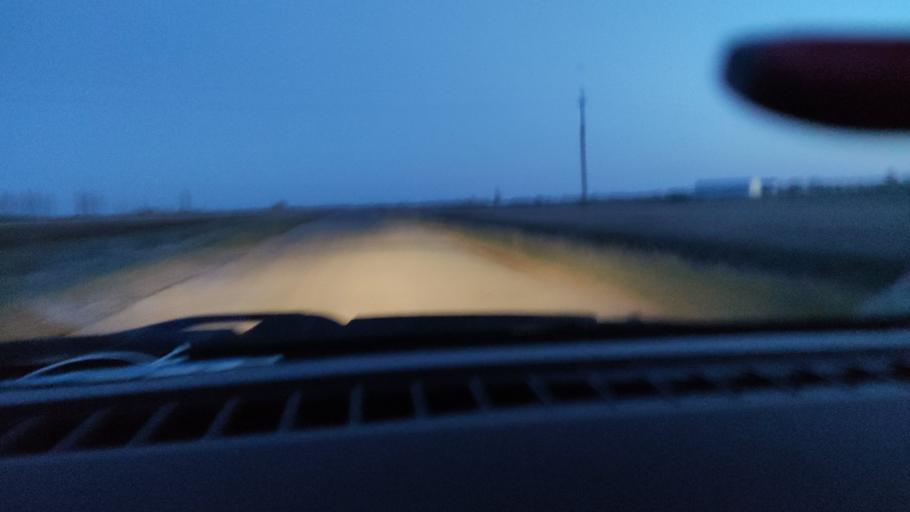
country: RU
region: Saratov
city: Rovnoye
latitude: 50.9356
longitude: 46.0944
